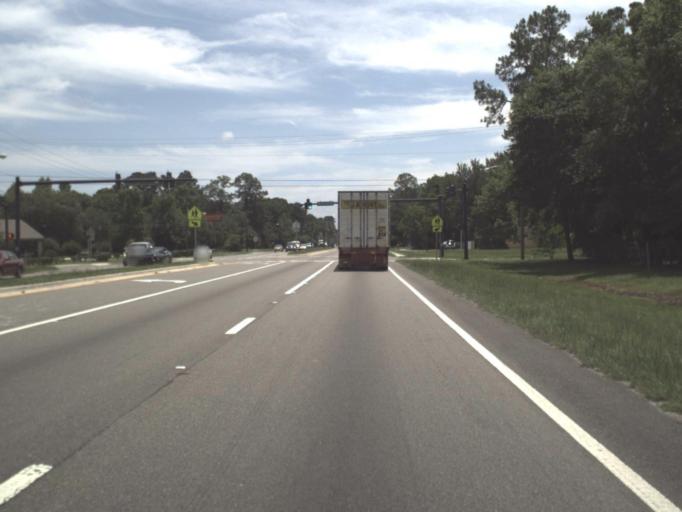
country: US
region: Florida
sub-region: Duval County
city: Jacksonville
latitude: 30.3819
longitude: -81.7306
